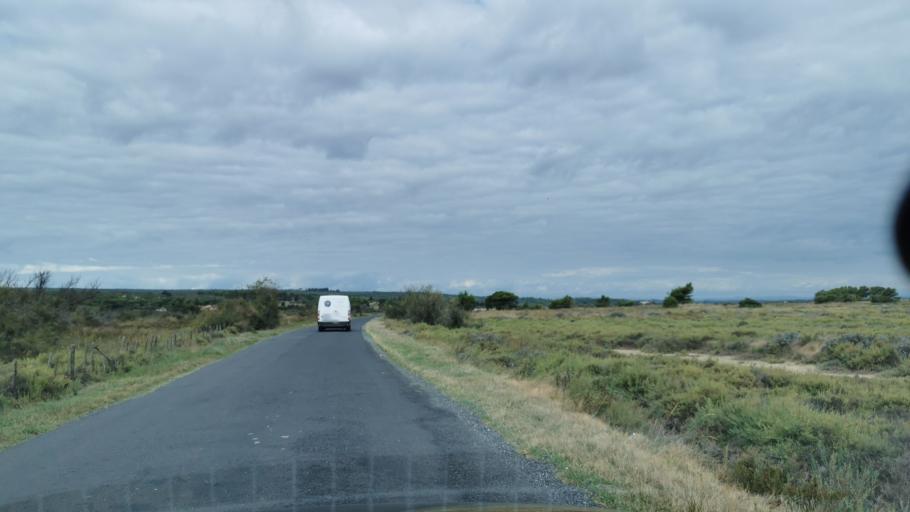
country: FR
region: Languedoc-Roussillon
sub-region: Departement de l'Aude
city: Fleury
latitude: 43.1966
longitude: 3.1971
